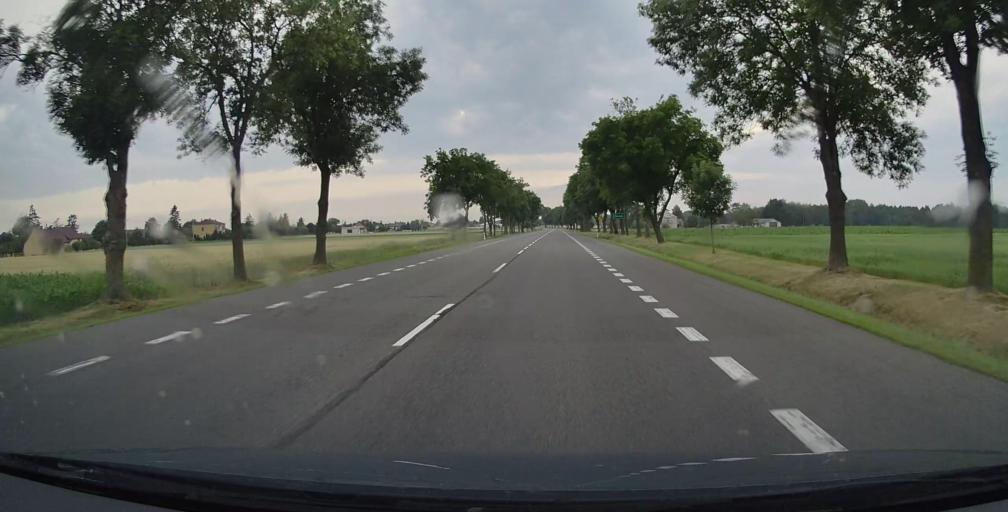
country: PL
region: Lublin Voivodeship
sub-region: Powiat lukowski
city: Trzebieszow
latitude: 52.0604
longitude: 22.5690
